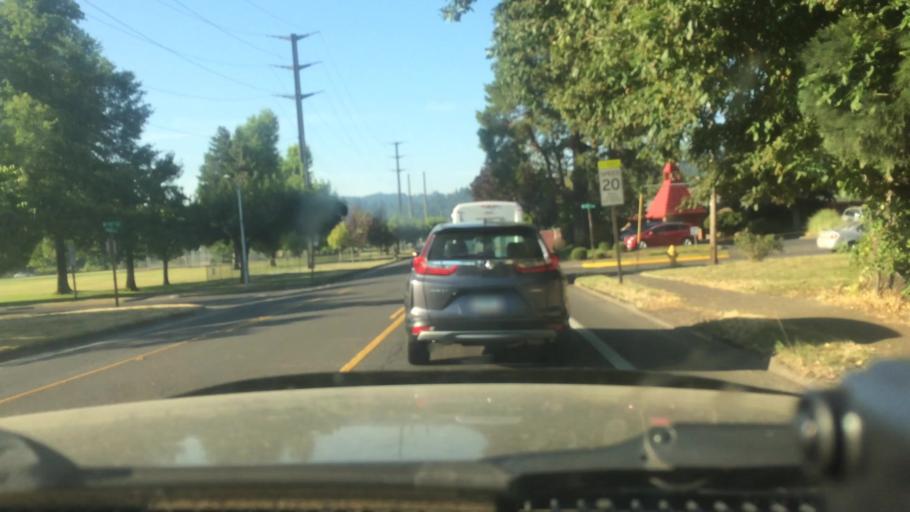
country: US
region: Oregon
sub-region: Lane County
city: Eugene
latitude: 44.0448
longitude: -123.1182
